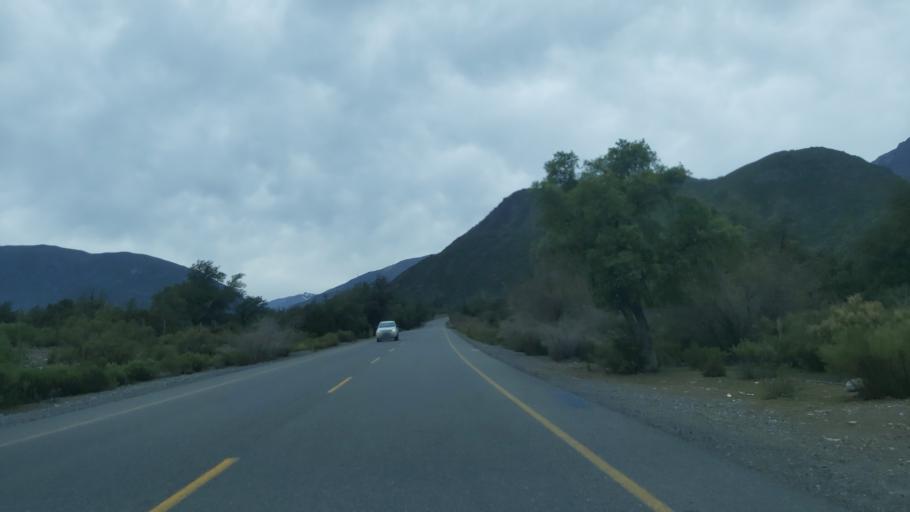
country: CL
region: Maule
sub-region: Provincia de Linares
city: Colbun
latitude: -35.8084
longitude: -70.8808
